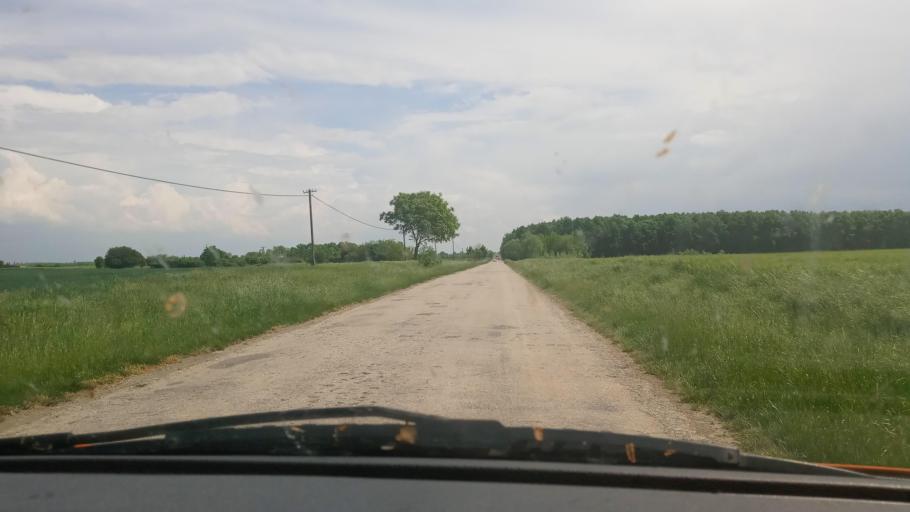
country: HU
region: Baranya
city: Siklos
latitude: 45.8076
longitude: 18.3425
